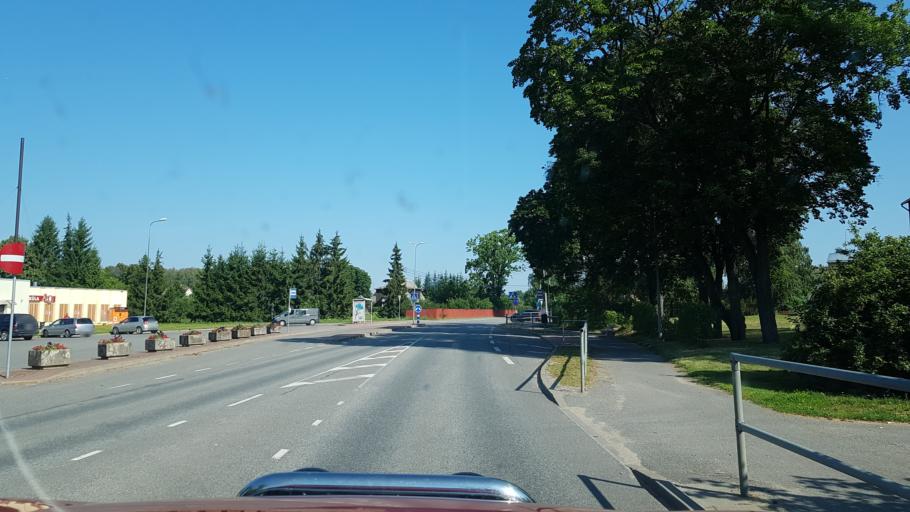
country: EE
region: Tartu
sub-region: Tartu linn
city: Tartu
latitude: 58.4192
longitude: 26.7628
